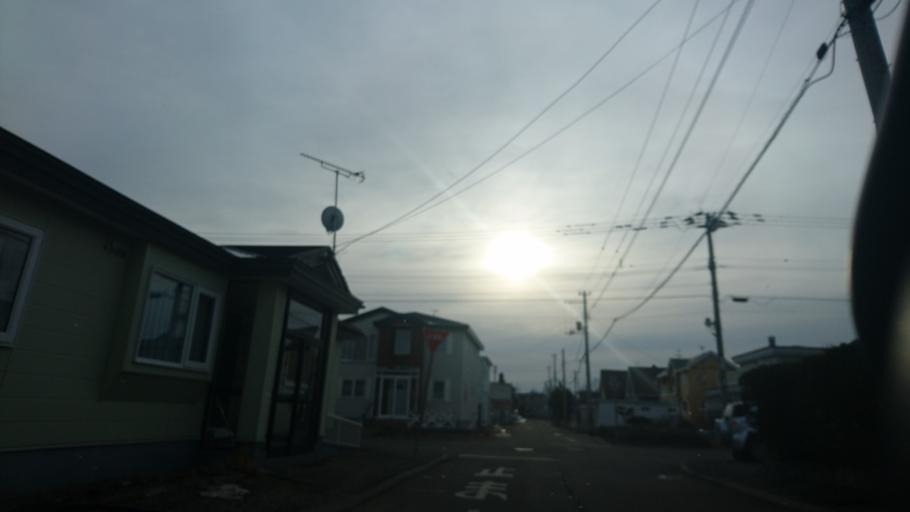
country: JP
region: Hokkaido
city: Otofuke
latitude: 43.0010
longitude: 143.1904
